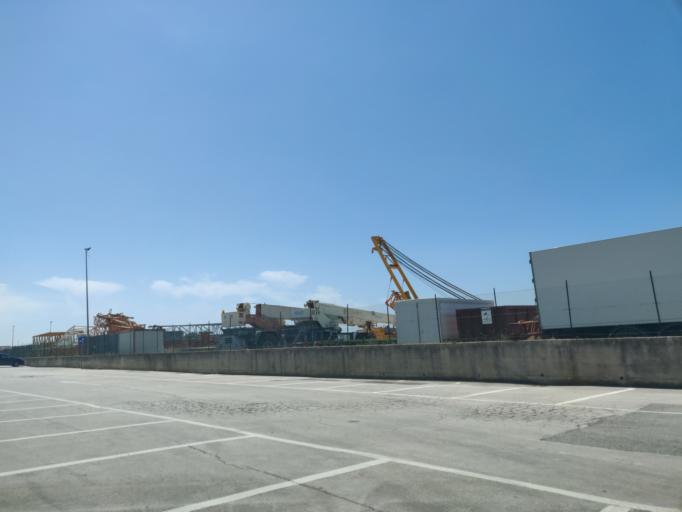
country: IT
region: Latium
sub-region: Citta metropolitana di Roma Capitale
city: Aurelia
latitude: 42.1242
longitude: 11.7682
